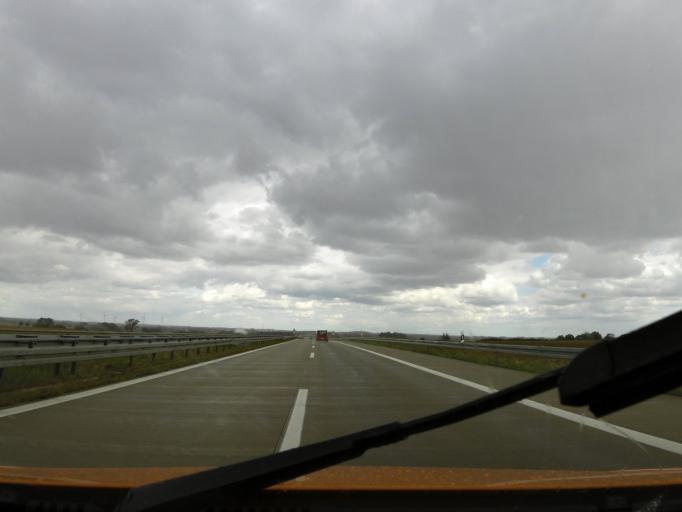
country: DE
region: Mecklenburg-Vorpommern
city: Penkun
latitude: 53.3075
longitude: 14.2280
